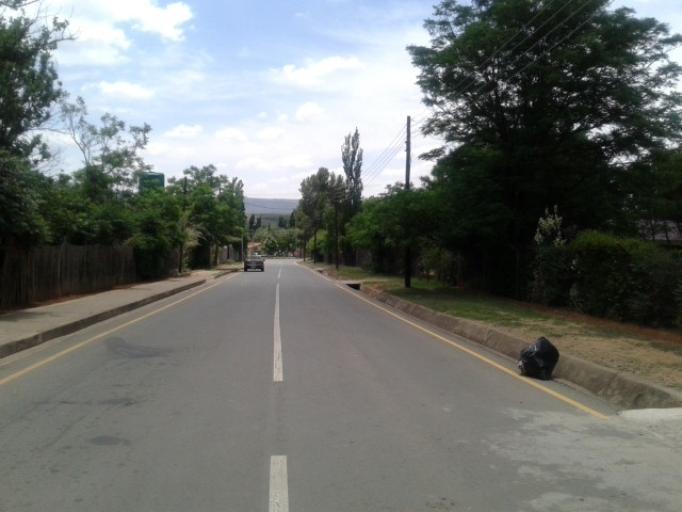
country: LS
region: Maseru
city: Maseru
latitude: -29.3042
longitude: 27.4714
